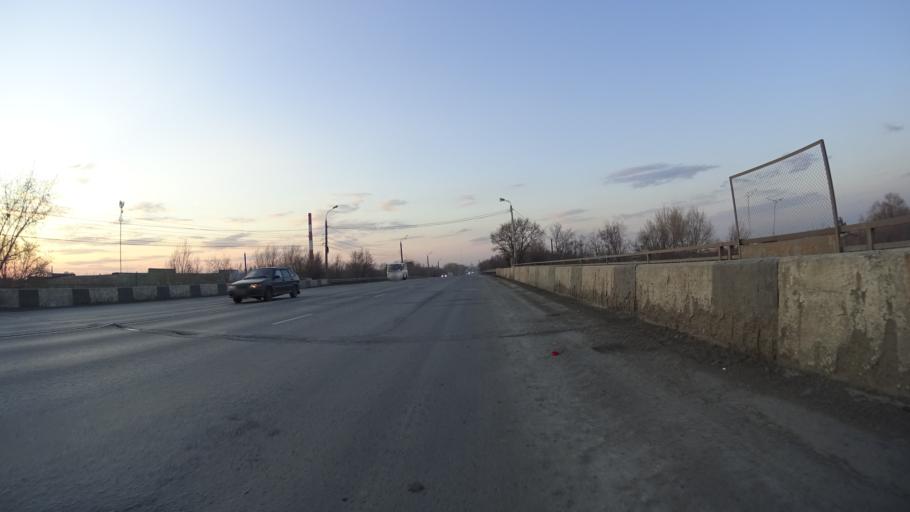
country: RU
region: Chelyabinsk
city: Novosineglazovskiy
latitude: 55.1021
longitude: 61.3876
